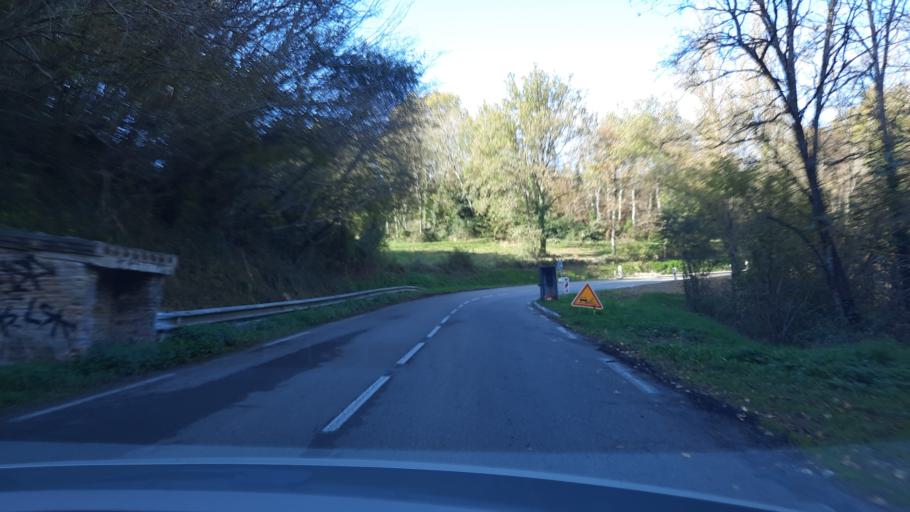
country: FR
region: Midi-Pyrenees
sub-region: Departement du Tarn-et-Garonne
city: Molieres
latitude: 44.1212
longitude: 1.3512
